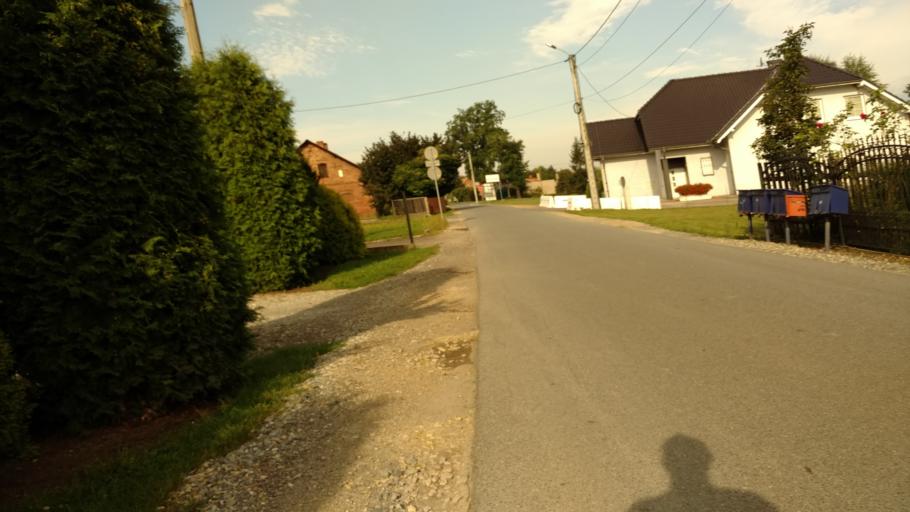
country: PL
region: Silesian Voivodeship
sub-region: Powiat pszczynski
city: Jankowice
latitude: 49.9979
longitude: 18.9775
